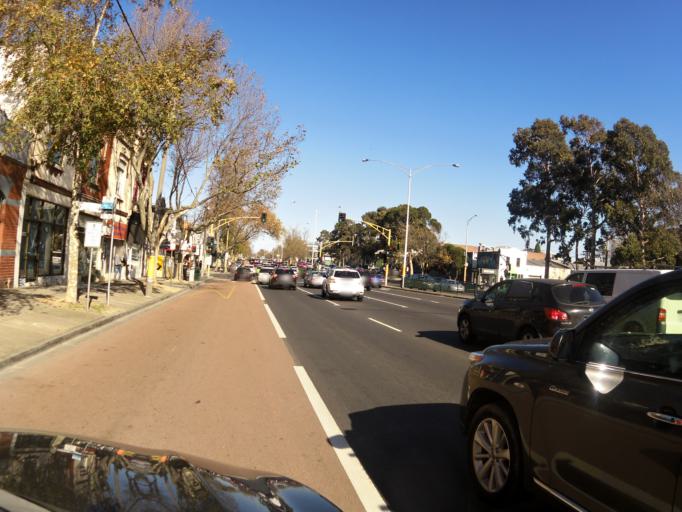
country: AU
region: Victoria
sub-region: Yarra
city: Clifton Hill
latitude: -37.8044
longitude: 144.9924
